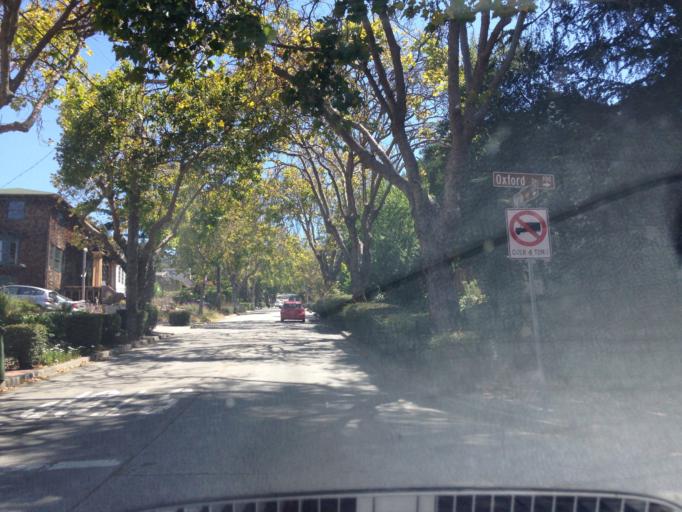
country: US
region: California
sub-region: Alameda County
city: Berkeley
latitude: 37.8916
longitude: -122.2701
